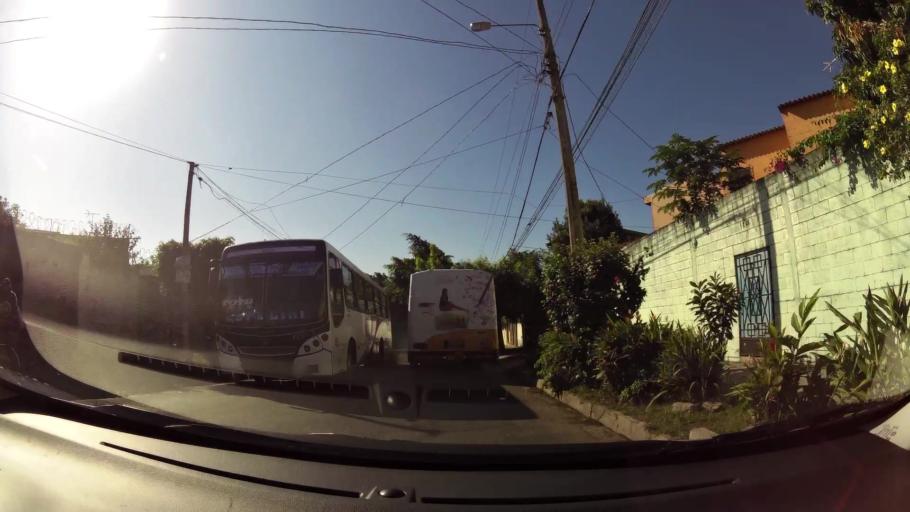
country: SV
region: La Libertad
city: Santa Tecla
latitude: 13.6832
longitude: -89.2934
